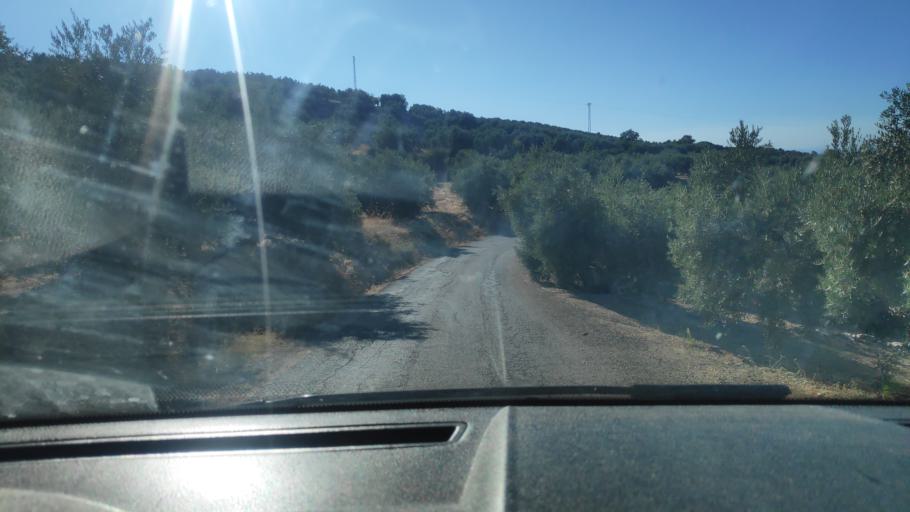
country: ES
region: Andalusia
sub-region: Provincia de Jaen
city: Torres
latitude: 37.7765
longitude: -3.5358
